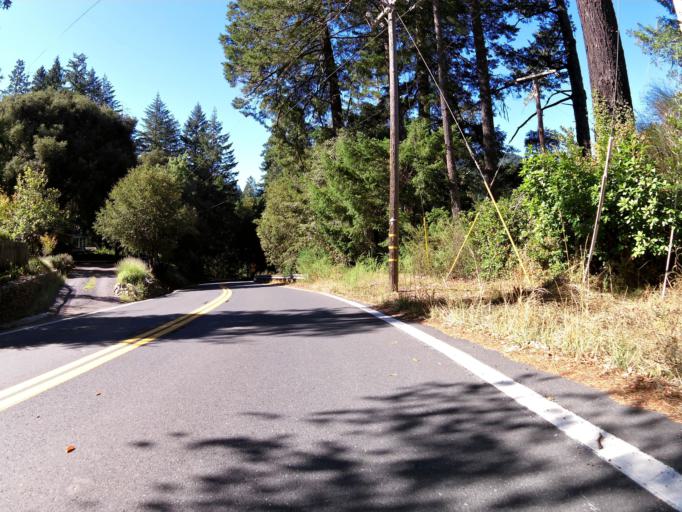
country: US
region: California
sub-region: Humboldt County
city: Redway
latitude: 39.8678
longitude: -123.7165
